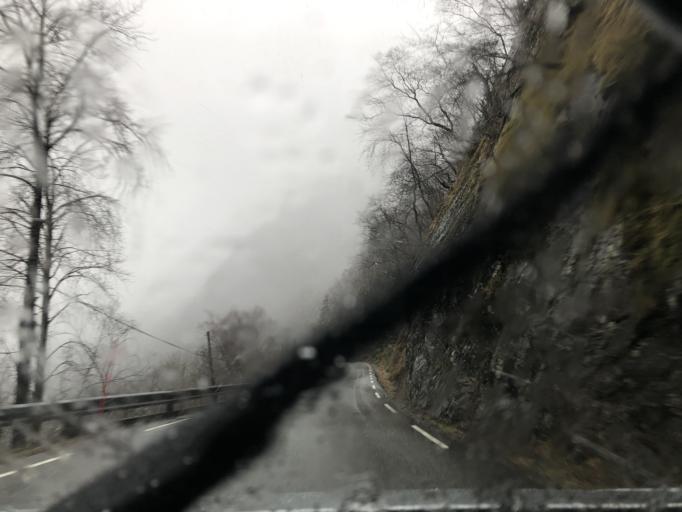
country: NO
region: Rogaland
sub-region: Suldal
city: Sand
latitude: 59.4064
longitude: 6.2056
